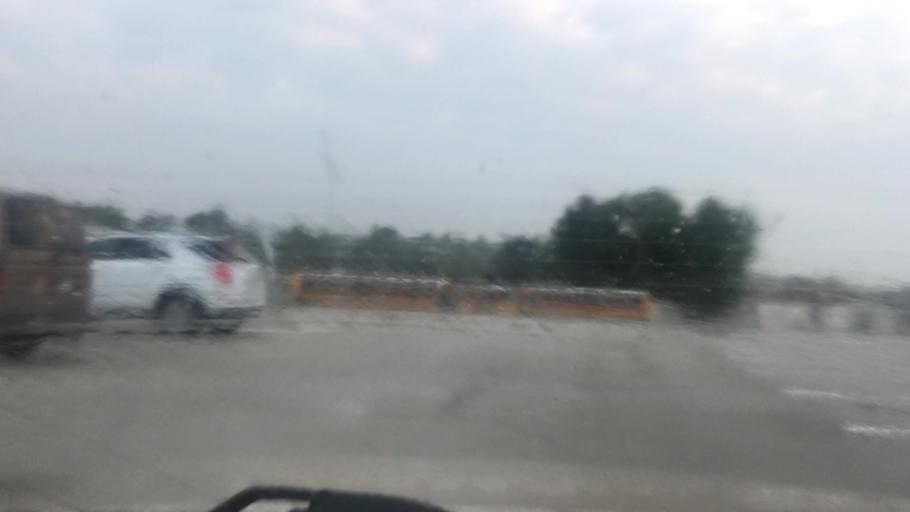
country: US
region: South Carolina
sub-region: Richland County
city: Lake Murray of Richland
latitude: 34.1530
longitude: -81.2052
